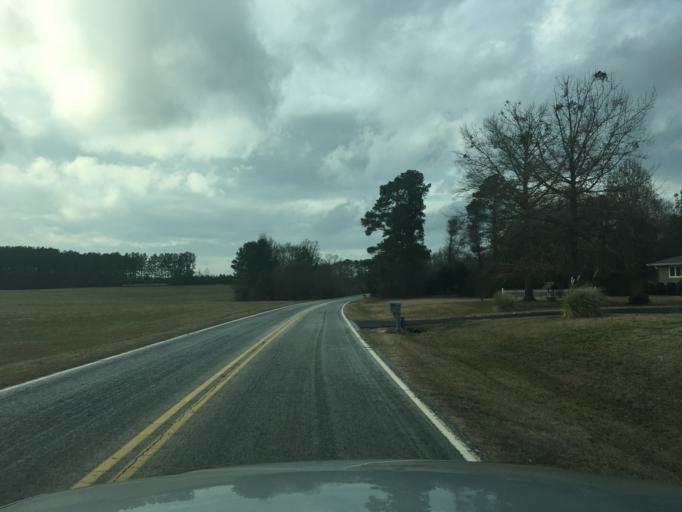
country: US
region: South Carolina
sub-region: Abbeville County
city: Abbeville
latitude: 34.2434
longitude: -82.4087
